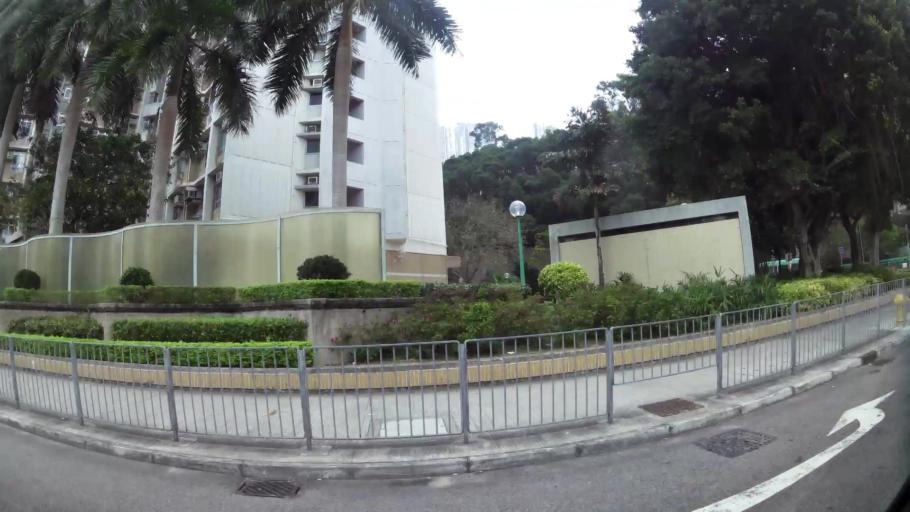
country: HK
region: Kowloon City
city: Kowloon
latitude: 22.3187
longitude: 114.2302
